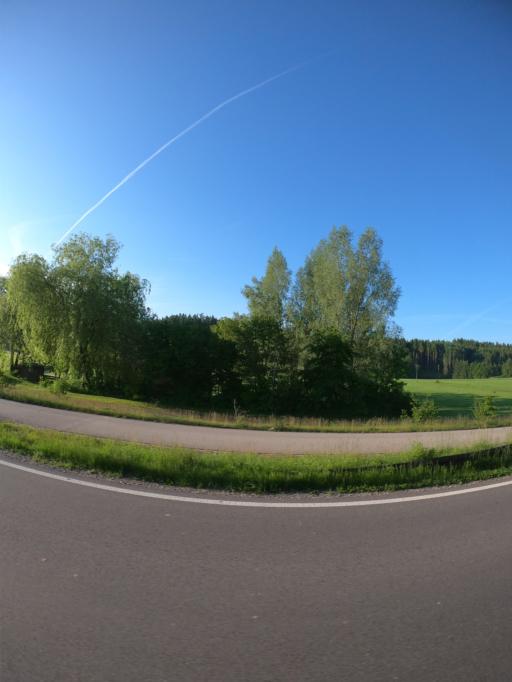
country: DE
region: Bavaria
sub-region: Upper Bavaria
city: Inning am Holz
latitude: 48.3413
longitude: 12.0975
